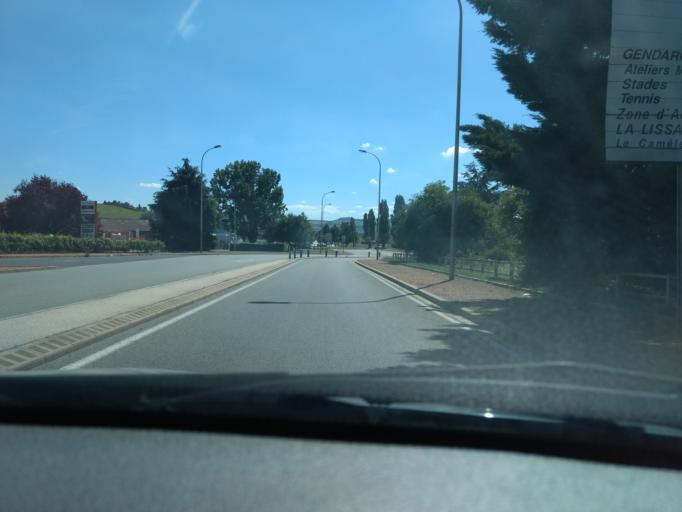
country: FR
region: Auvergne
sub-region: Departement du Puy-de-Dome
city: Pont-du-Chateau
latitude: 45.7935
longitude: 3.2286
